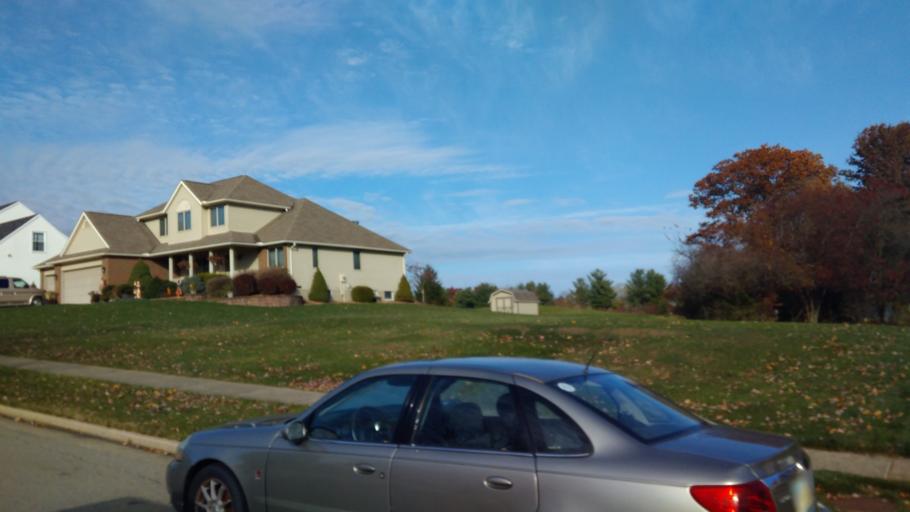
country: US
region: Ohio
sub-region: Richland County
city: Lexington
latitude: 40.6990
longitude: -82.5326
